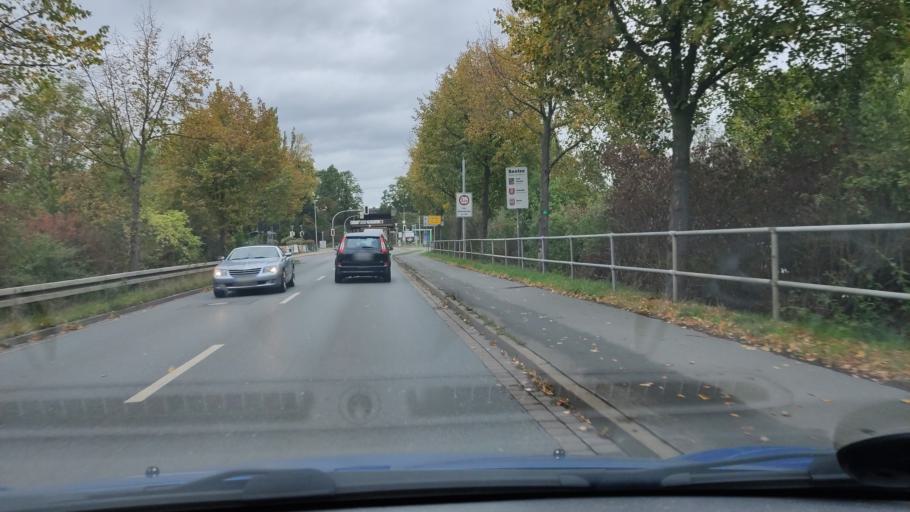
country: DE
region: Lower Saxony
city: Seelze
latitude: 52.3924
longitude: 9.6507
